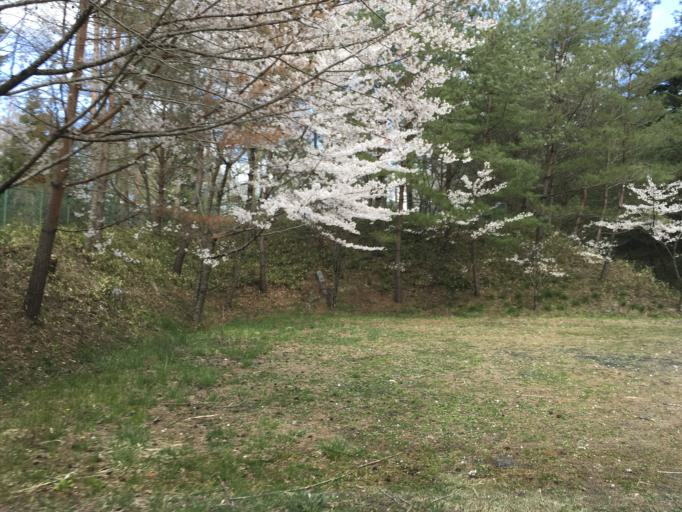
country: JP
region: Iwate
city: Ichinoseki
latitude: 38.7512
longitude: 141.2724
